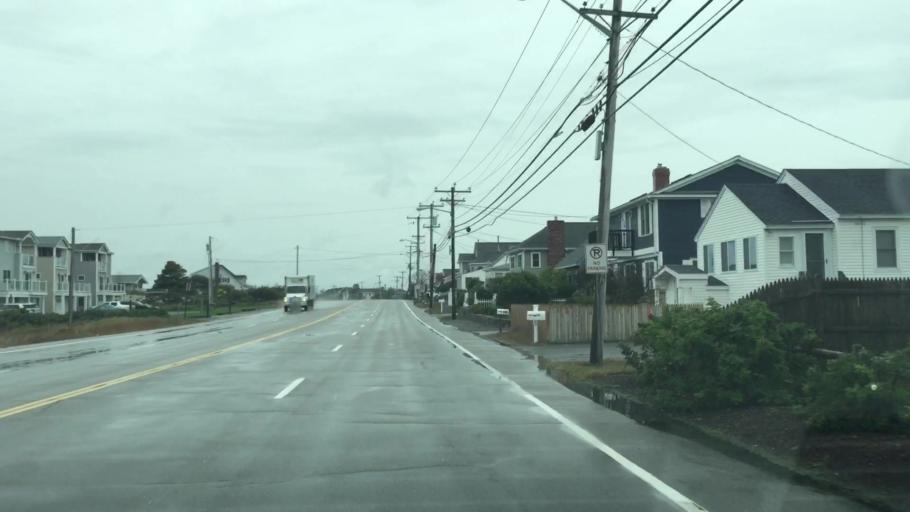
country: US
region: New Hampshire
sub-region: Rockingham County
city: Hampton Beach
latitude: 42.8781
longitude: -70.8183
